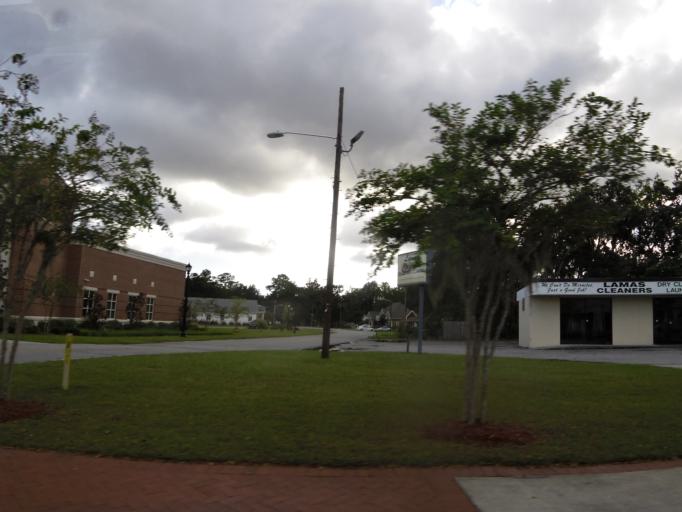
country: US
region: Georgia
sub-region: Liberty County
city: Hinesville
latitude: 31.8507
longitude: -81.5990
